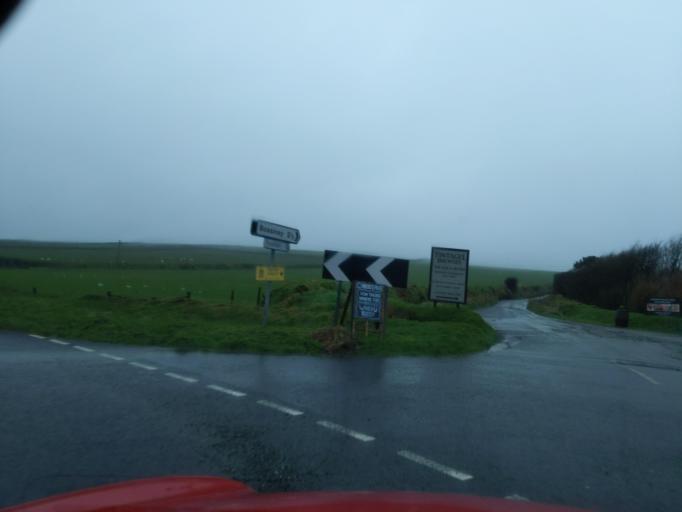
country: GB
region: England
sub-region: Cornwall
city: Camelford
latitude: 50.6461
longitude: -4.6986
